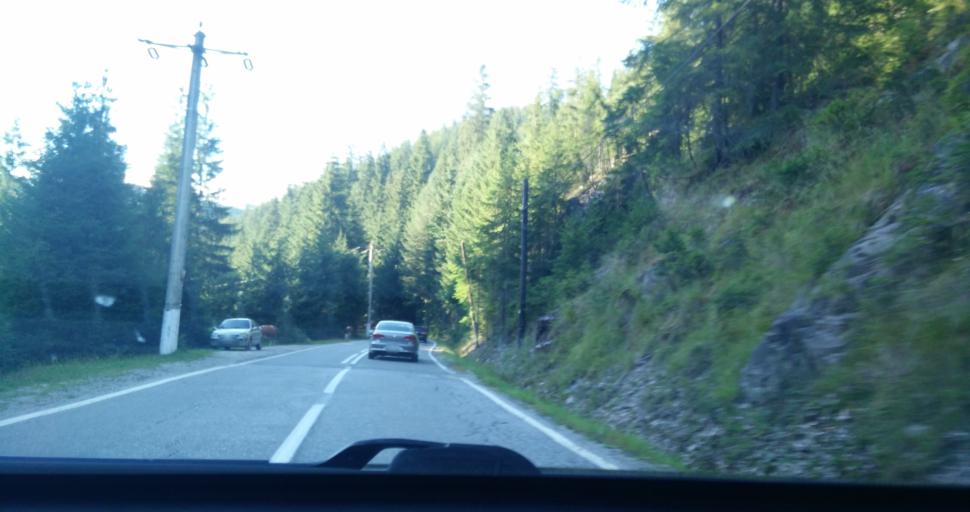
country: RO
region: Alba
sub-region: Comuna Garda de Sus
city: Garda de Sus
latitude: 46.4618
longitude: 22.7892
